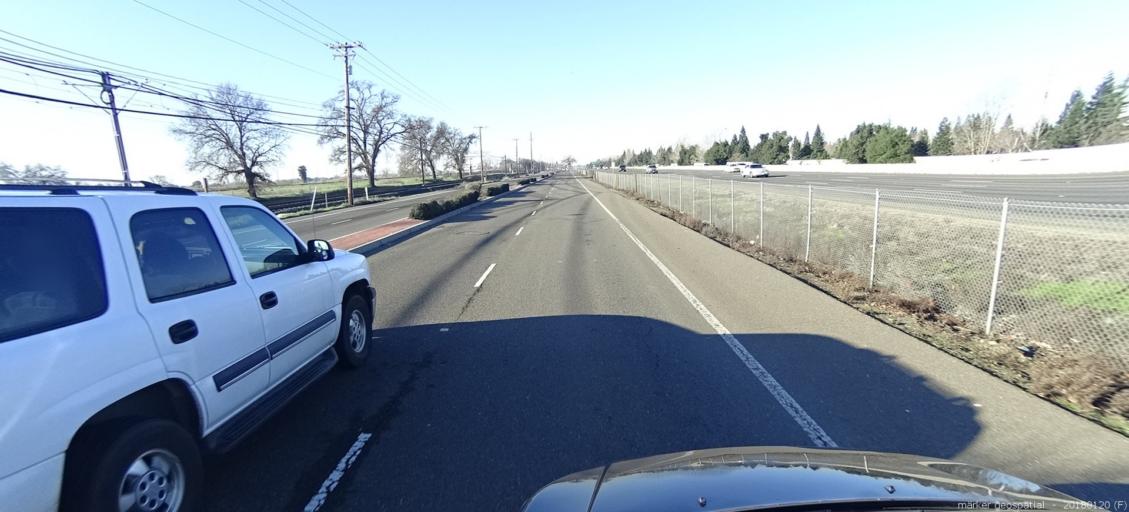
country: US
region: California
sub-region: Sacramento County
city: Gold River
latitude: 38.6234
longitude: -121.2313
